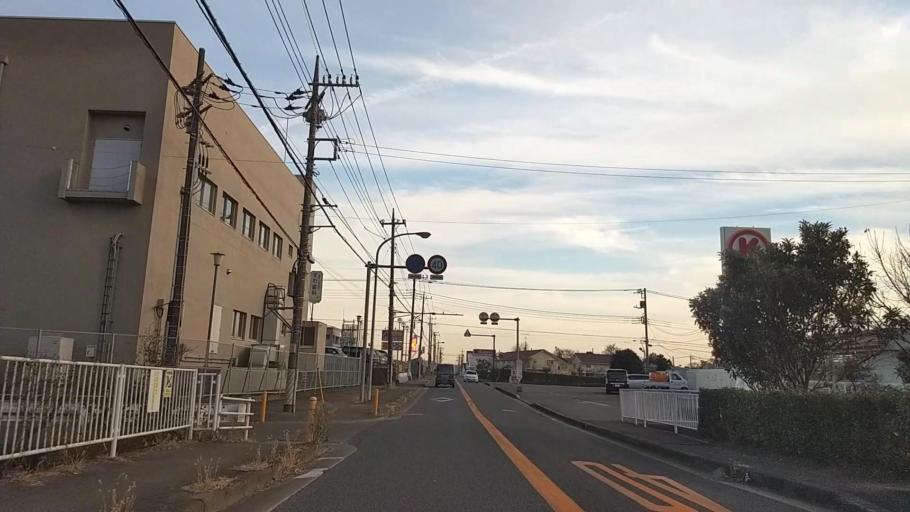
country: JP
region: Kanagawa
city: Atsugi
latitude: 35.4840
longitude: 139.3318
